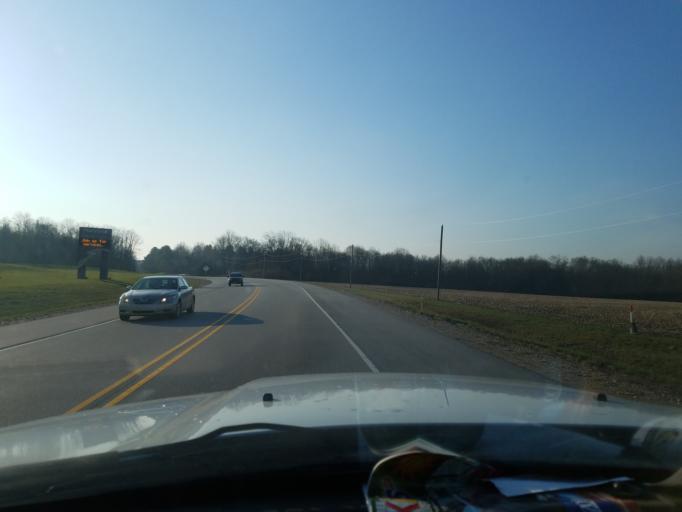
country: US
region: Indiana
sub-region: Vigo County
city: Terre Haute
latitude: 39.4097
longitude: -87.3311
